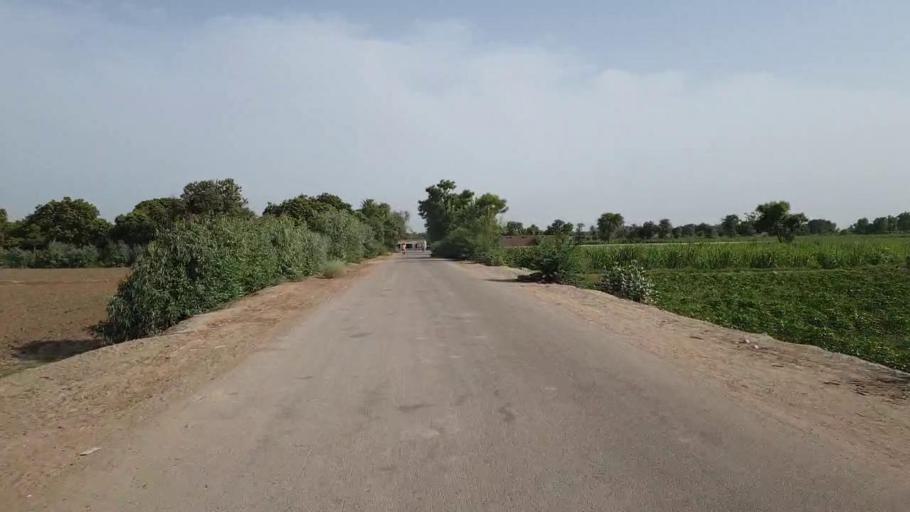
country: PK
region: Sindh
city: Sakrand
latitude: 26.2464
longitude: 68.2845
